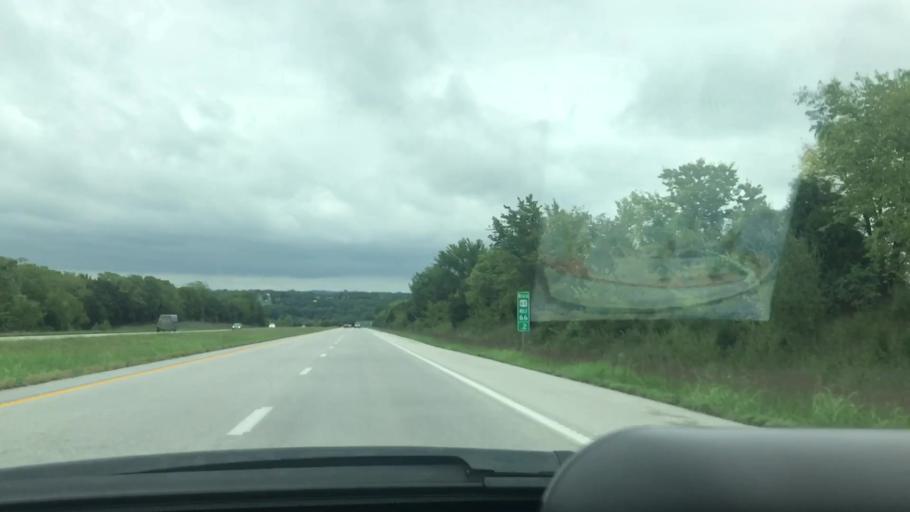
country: US
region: Missouri
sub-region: Greene County
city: Fair Grove
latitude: 37.4026
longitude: -93.1482
